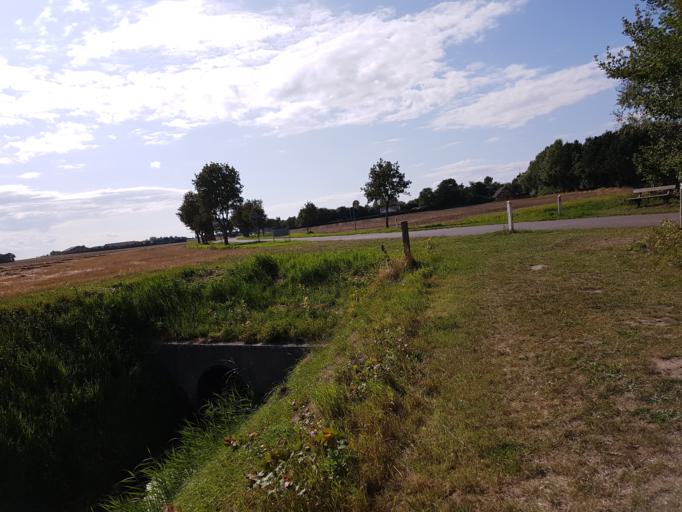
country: DK
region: Zealand
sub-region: Guldborgsund Kommune
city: Nykobing Falster
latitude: 54.6007
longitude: 11.9495
